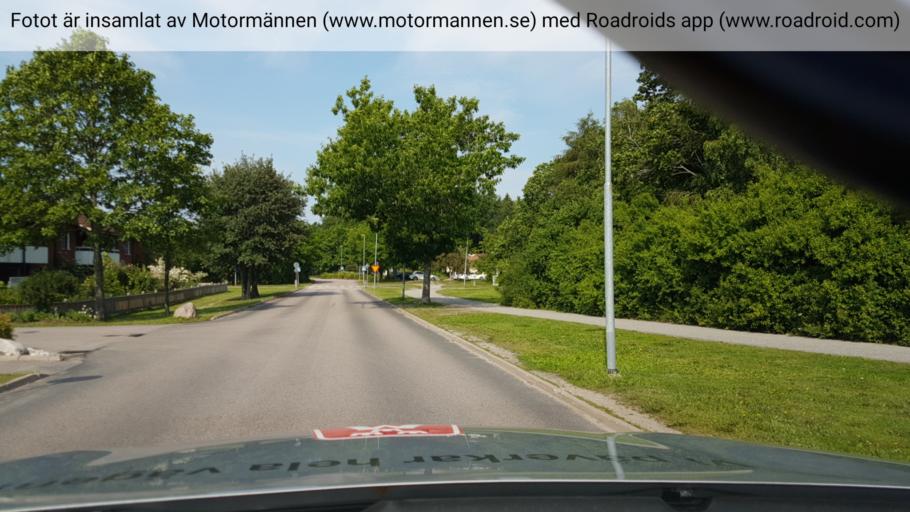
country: SE
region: Vaestmanland
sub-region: Vasteras
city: Vasteras
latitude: 59.6420
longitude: 16.5406
